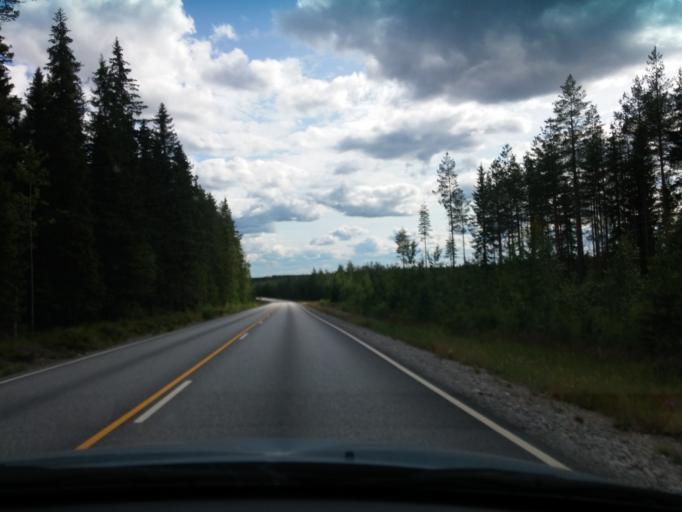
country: FI
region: Central Finland
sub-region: Keuruu
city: Multia
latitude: 62.5438
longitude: 24.6266
